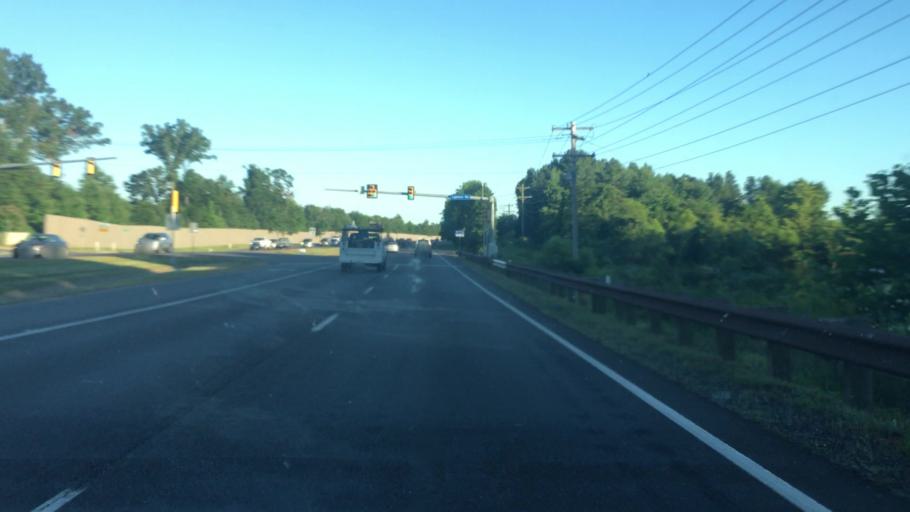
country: US
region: Virginia
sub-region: Prince William County
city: Haymarket
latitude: 38.8368
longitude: -77.6342
